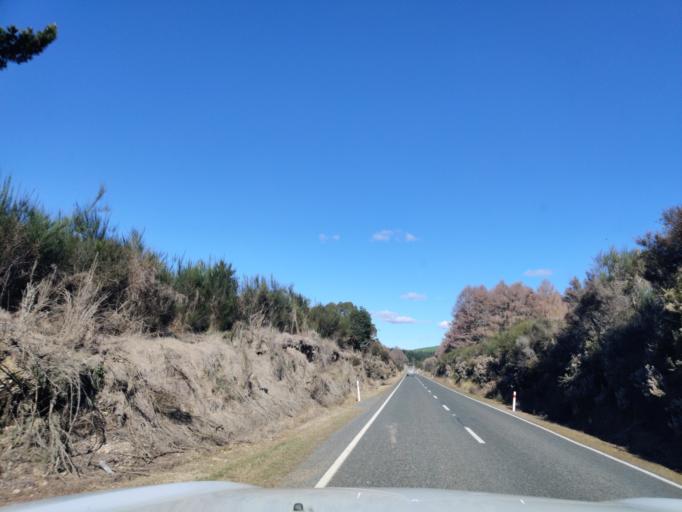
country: NZ
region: Waikato
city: Turangi
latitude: -38.8421
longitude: 175.6859
